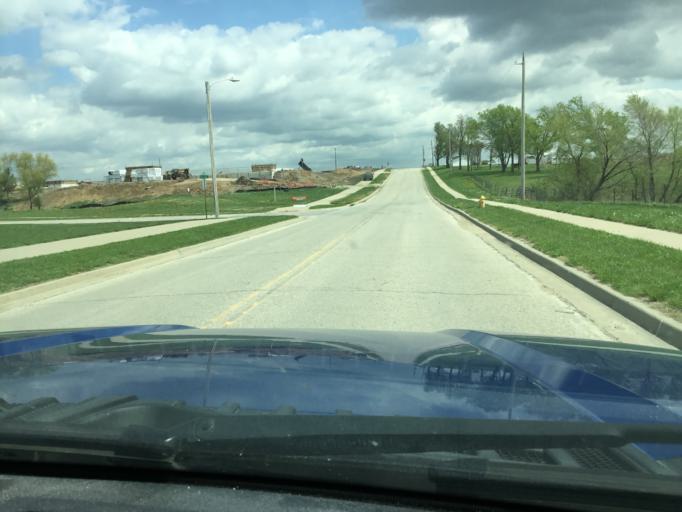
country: US
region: Kansas
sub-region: Douglas County
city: Eudora
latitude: 38.9132
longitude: -95.0965
